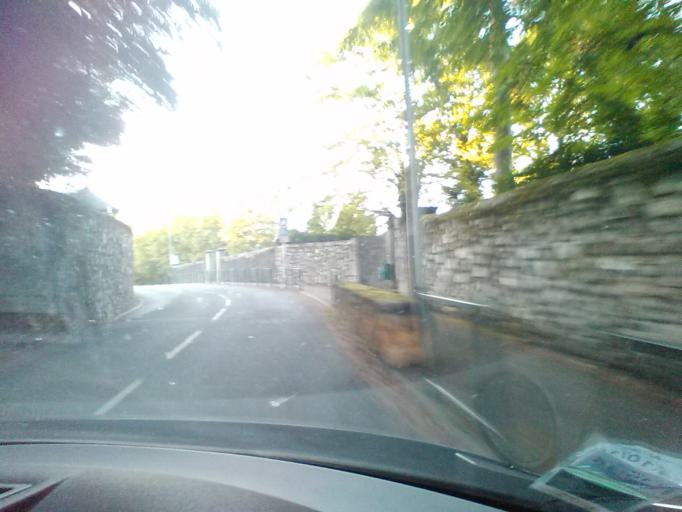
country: FR
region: Rhone-Alpes
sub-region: Departement de la Savoie
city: Chambery
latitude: 45.5592
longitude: 5.9390
